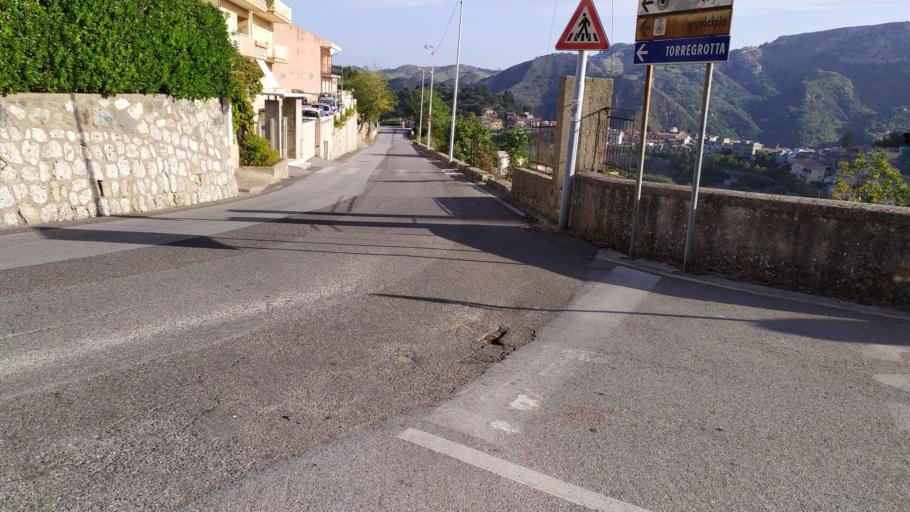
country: IT
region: Sicily
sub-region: Messina
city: Monforte San Giorgio
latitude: 38.1570
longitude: 15.3791
